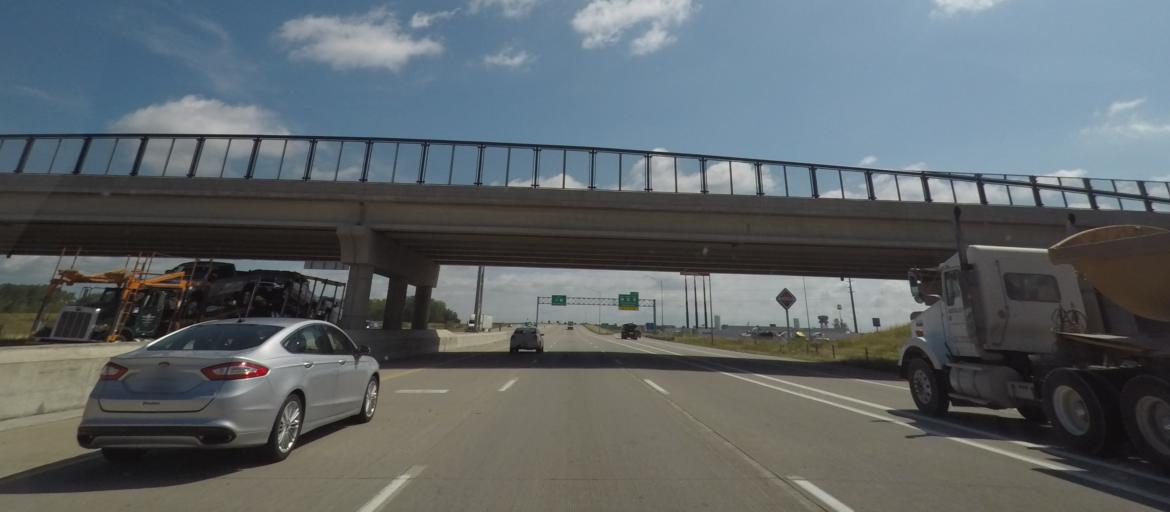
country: US
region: Iowa
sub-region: Polk County
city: Altoona
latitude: 41.6619
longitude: -93.5035
